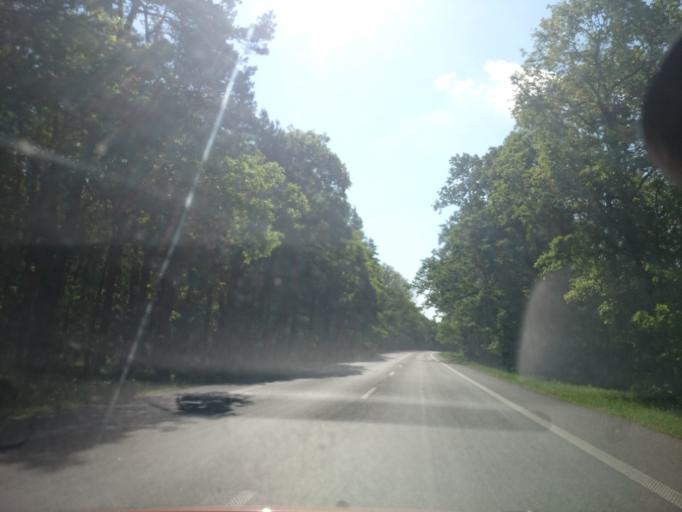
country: PL
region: Opole Voivodeship
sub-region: Powiat opolski
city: Tarnow Opolski
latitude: 50.6180
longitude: 18.0615
